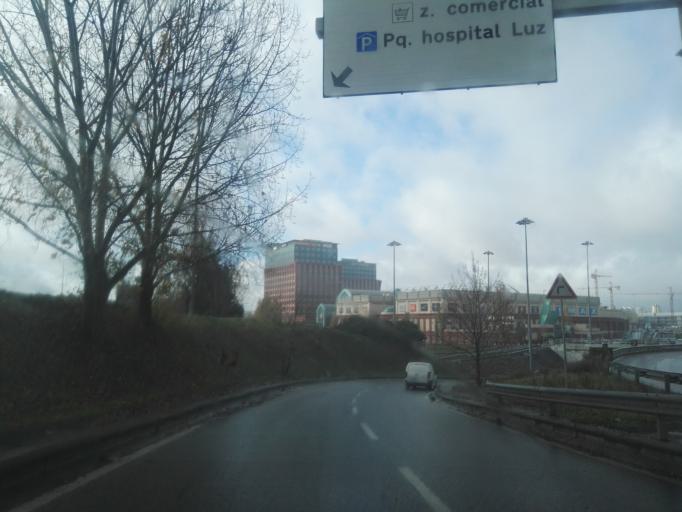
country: PT
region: Lisbon
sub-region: Odivelas
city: Pontinha
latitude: 38.7558
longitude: -9.1837
